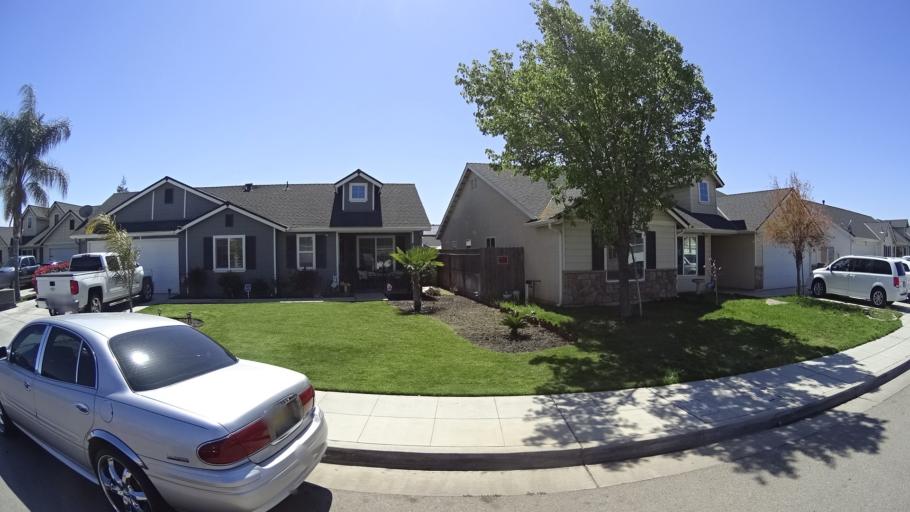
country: US
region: California
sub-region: Fresno County
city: West Park
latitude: 36.7770
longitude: -119.8842
